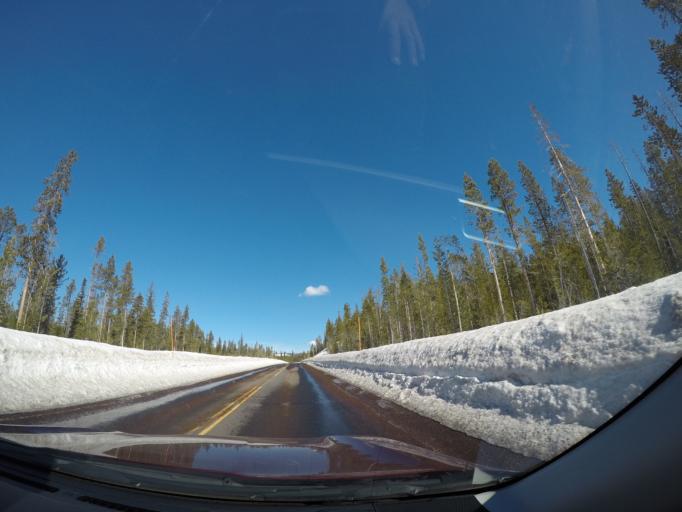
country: US
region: Oregon
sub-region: Deschutes County
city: Sunriver
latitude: 43.9588
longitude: -121.6157
